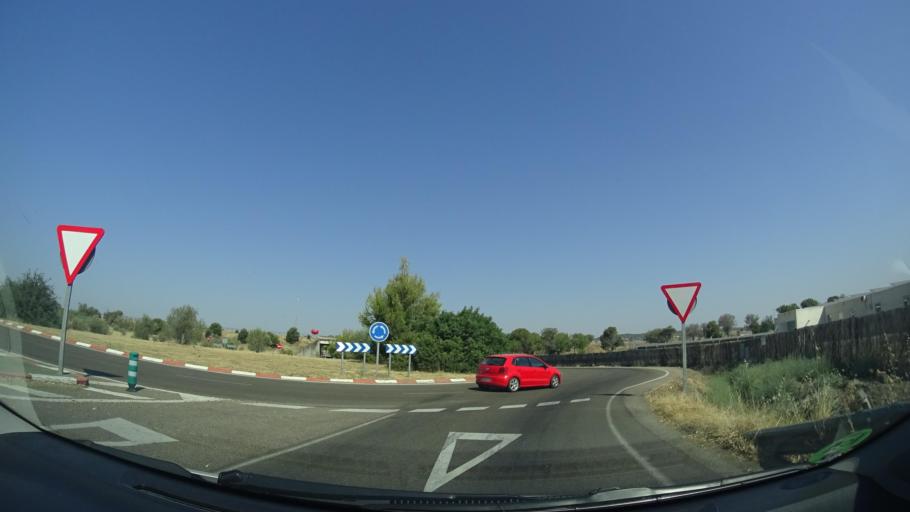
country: ES
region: Extremadura
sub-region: Provincia de Caceres
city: Miajadas
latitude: 39.1347
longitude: -5.9431
